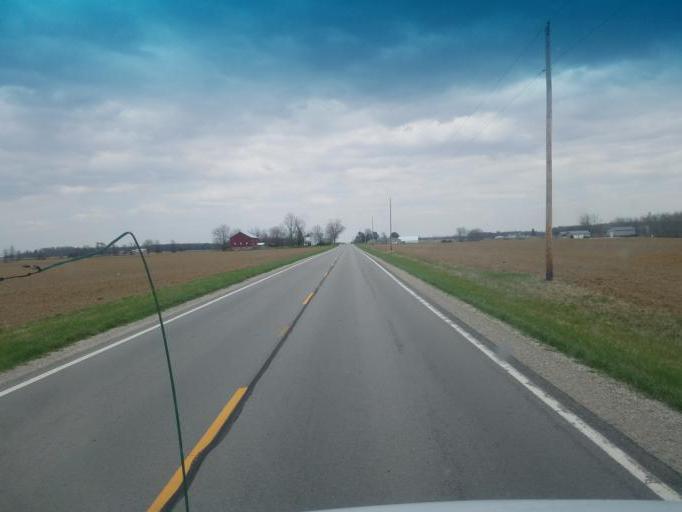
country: US
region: Ohio
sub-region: Seneca County
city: Tiffin
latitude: 40.9500
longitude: -83.1069
